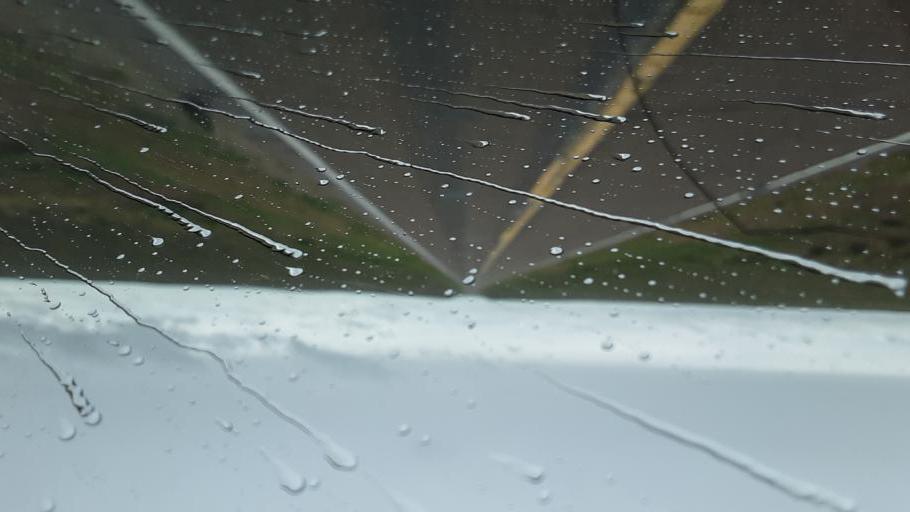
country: US
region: Colorado
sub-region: Lincoln County
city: Hugo
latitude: 38.8494
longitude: -103.2463
